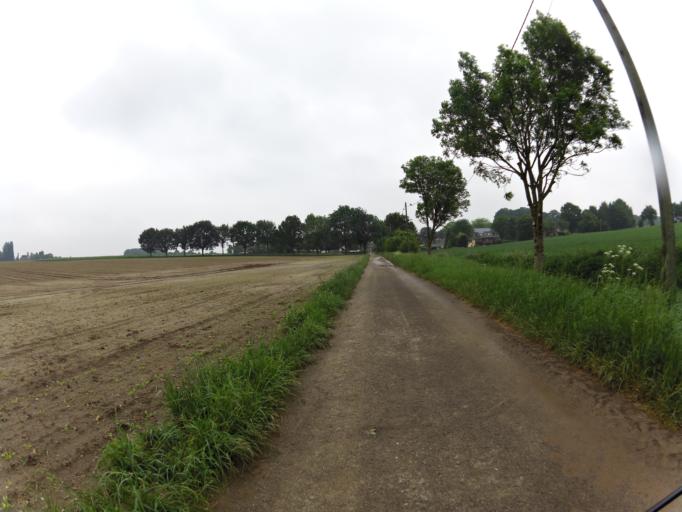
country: DE
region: North Rhine-Westphalia
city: Geilenkirchen
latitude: 50.9670
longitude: 6.0760
